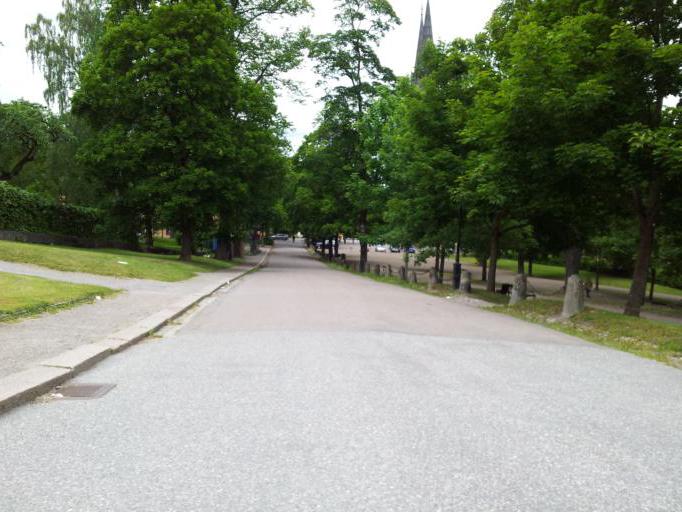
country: SE
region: Uppsala
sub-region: Uppsala Kommun
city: Uppsala
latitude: 59.8556
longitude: 17.6321
